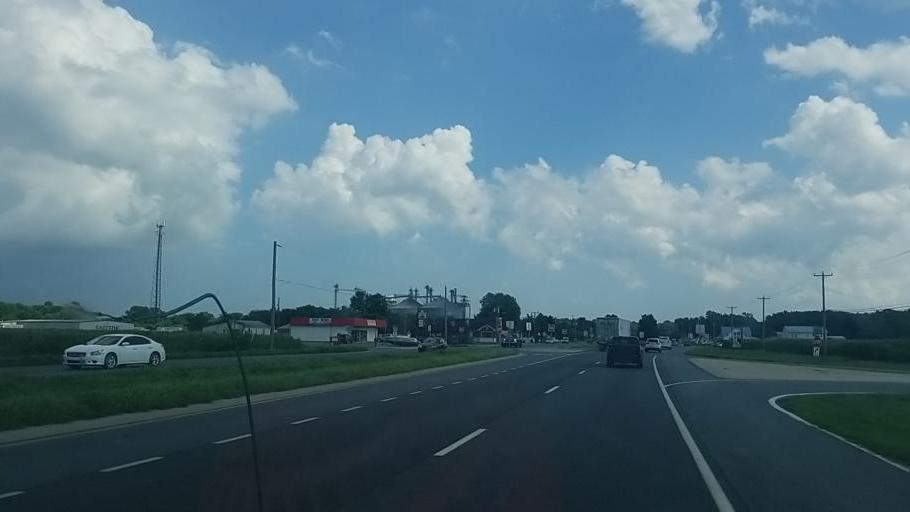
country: US
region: Delaware
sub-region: Sussex County
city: Selbyville
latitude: 38.5218
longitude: -75.2432
